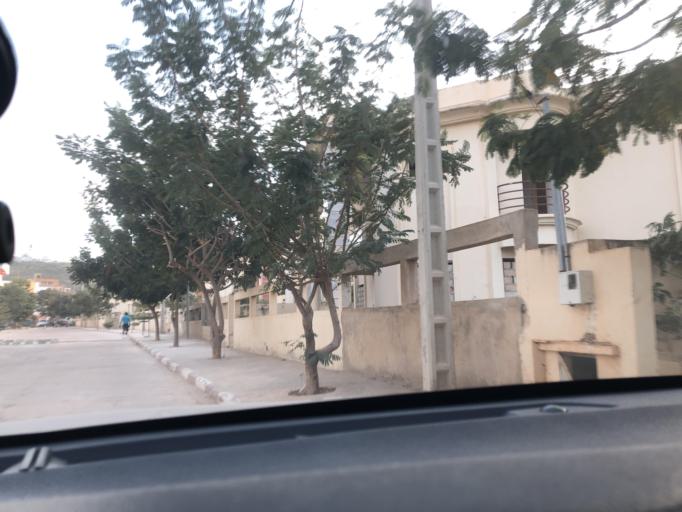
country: SN
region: Dakar
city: Mermoz Boabab
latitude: 14.7302
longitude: -17.5021
